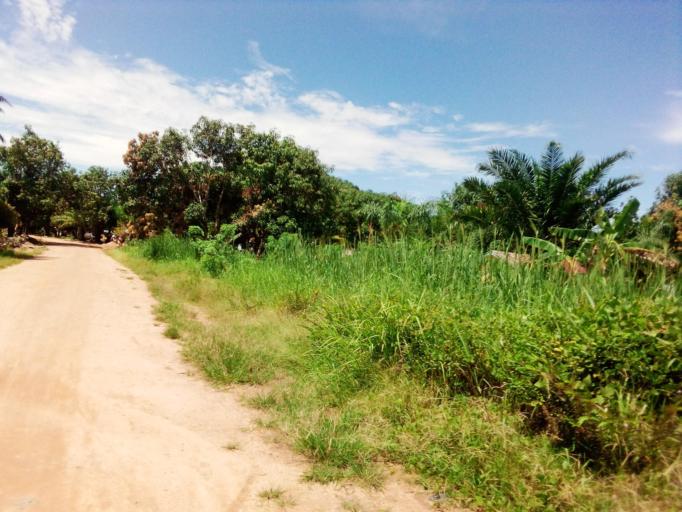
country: SL
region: Eastern Province
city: Koidu
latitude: 8.6518
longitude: -10.9470
